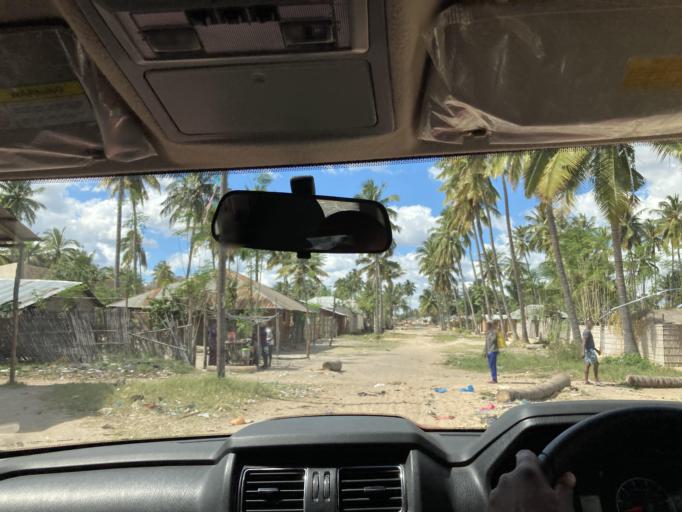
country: MZ
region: Cabo Delgado
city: Montepuez
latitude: -13.1301
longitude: 39.0099
